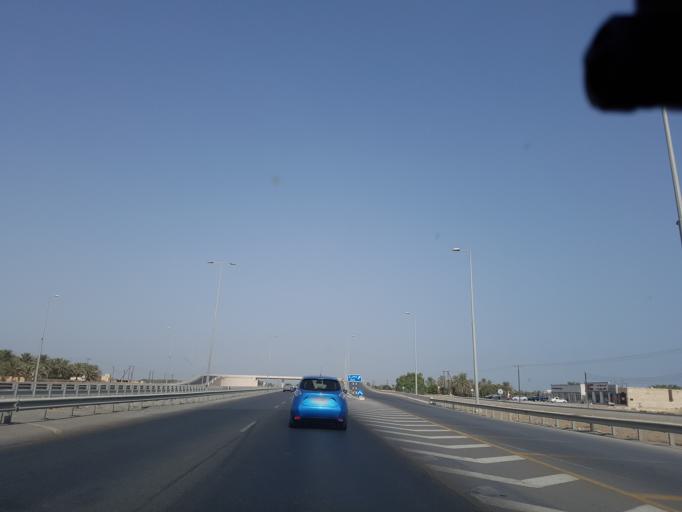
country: OM
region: Al Batinah
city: Barka'
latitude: 23.7273
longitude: 57.7185
